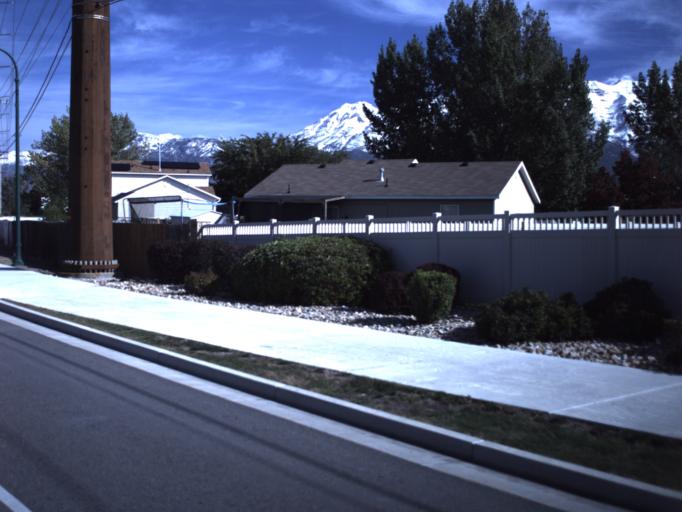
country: US
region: Utah
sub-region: Utah County
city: Orem
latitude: 40.2846
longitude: -111.7335
